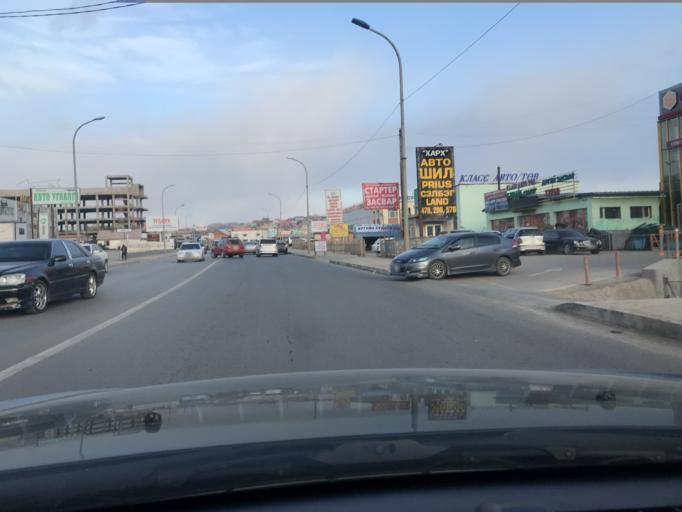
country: MN
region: Ulaanbaatar
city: Ulaanbaatar
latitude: 47.9240
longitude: 106.9924
